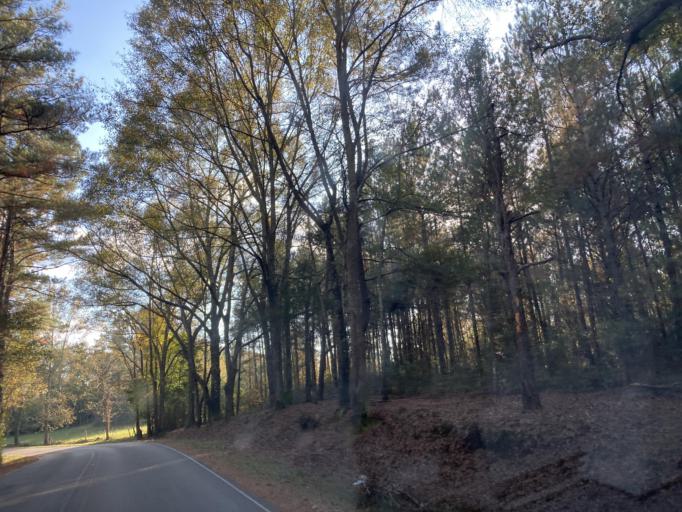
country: US
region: Mississippi
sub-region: Lamar County
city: Sumrall
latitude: 31.4007
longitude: -89.6501
